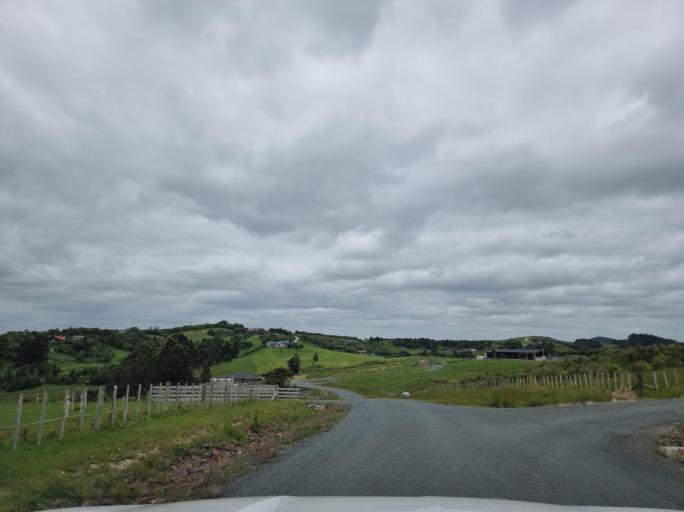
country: NZ
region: Auckland
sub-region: Auckland
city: Wellsford
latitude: -36.1724
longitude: 174.5587
